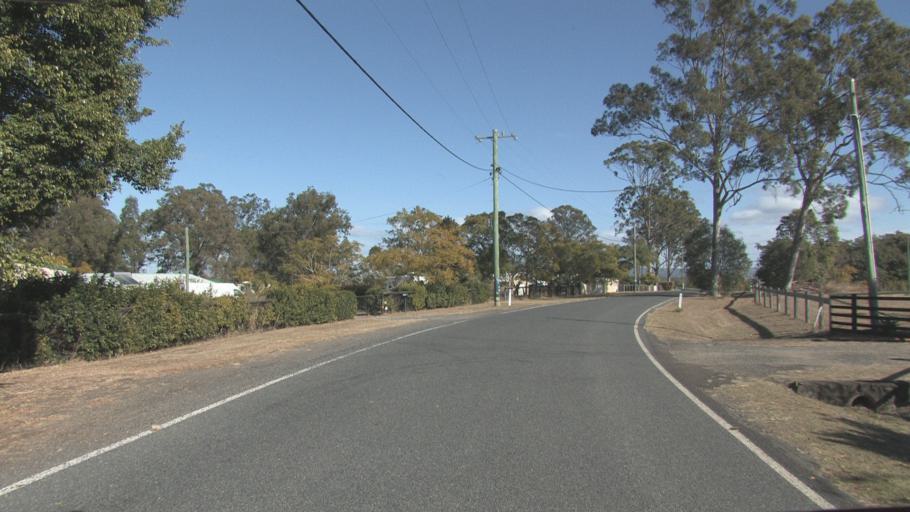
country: AU
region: Queensland
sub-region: Logan
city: Cedar Vale
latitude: -27.8771
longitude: 152.9840
